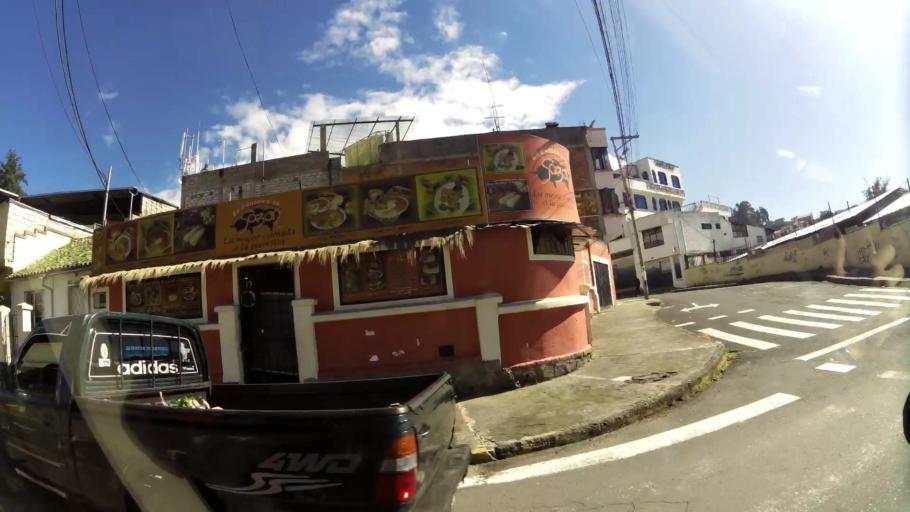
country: EC
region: Pichincha
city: Quito
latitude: -0.2362
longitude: -78.5305
